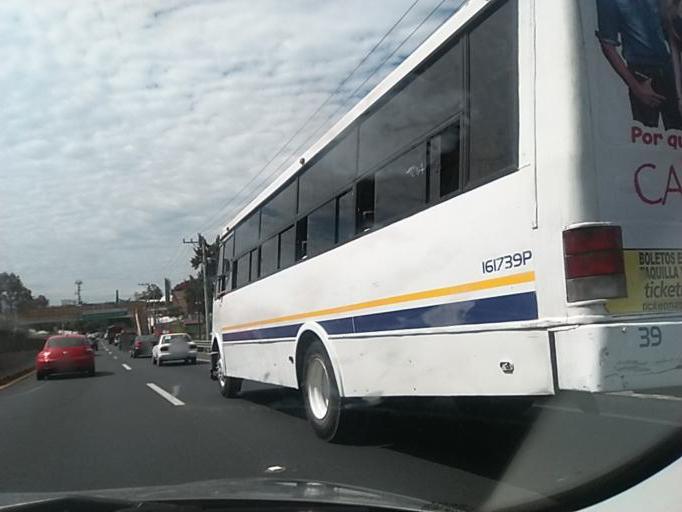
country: MX
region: Morelos
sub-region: Cuernavaca
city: Cuernavaca
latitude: 18.8975
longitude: -99.2257
